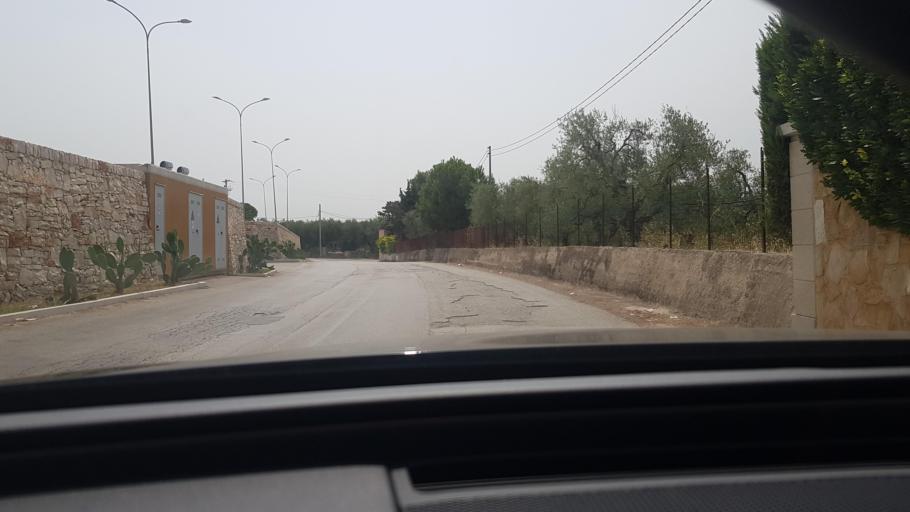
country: IT
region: Apulia
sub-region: Provincia di Barletta - Andria - Trani
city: Andria
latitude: 41.2295
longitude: 16.2683
